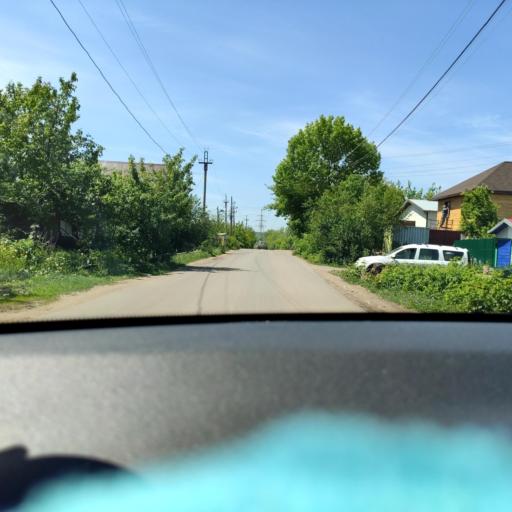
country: RU
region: Samara
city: Petra-Dubrava
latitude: 53.2875
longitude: 50.2942
